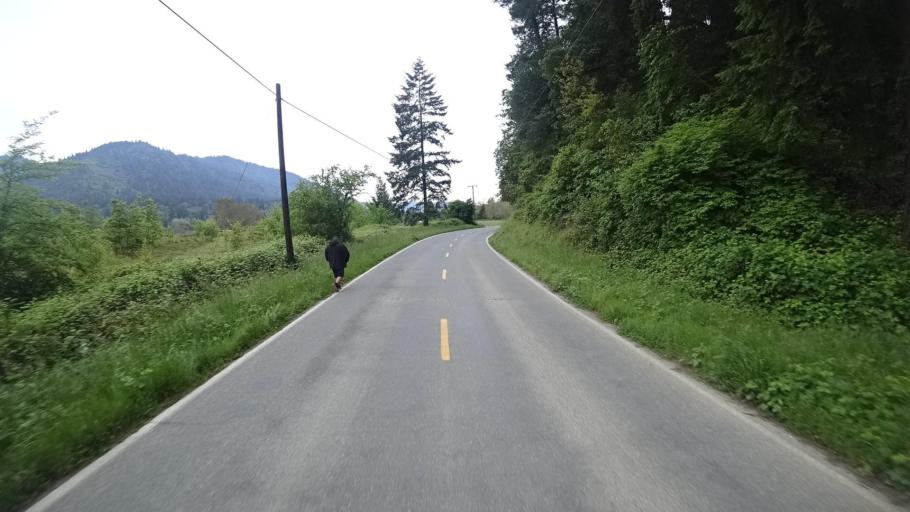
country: US
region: California
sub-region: Humboldt County
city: Willow Creek
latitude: 41.0760
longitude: -123.6951
